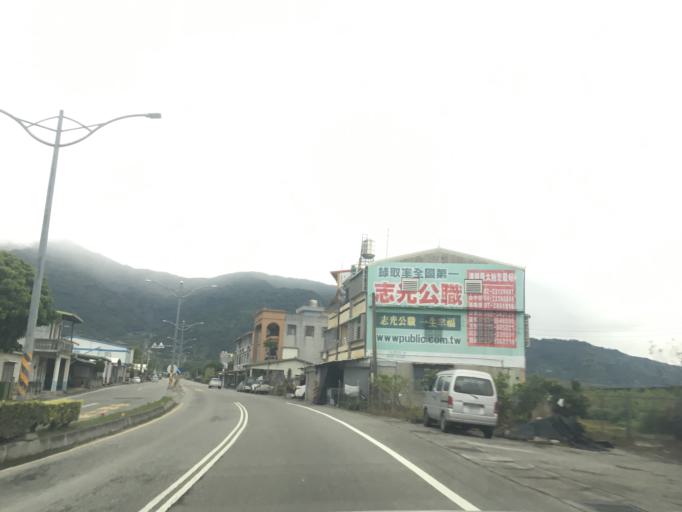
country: TW
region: Taiwan
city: Taitung City
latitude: 22.6946
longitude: 121.0456
